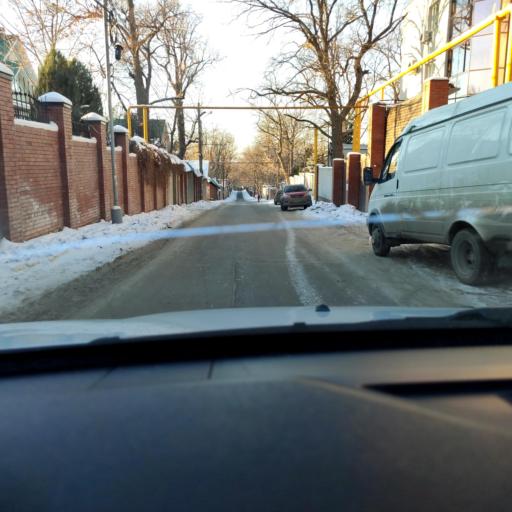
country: RU
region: Samara
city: Samara
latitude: 53.2621
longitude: 50.1902
